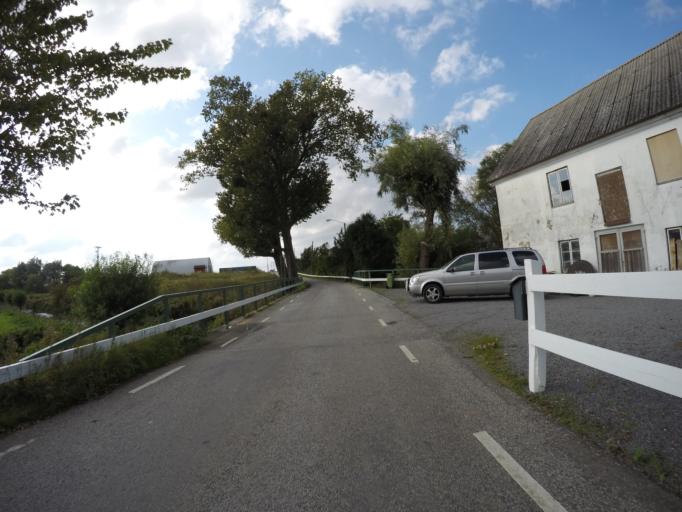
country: SE
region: Skane
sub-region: Staffanstorps Kommun
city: Hjaerup
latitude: 55.6041
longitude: 13.1430
